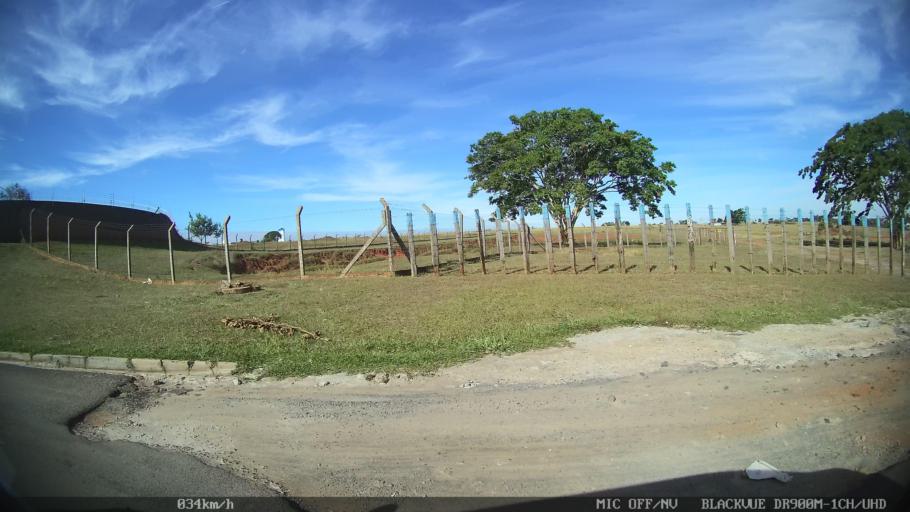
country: BR
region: Sao Paulo
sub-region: Sao Jose Do Rio Preto
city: Sao Jose do Rio Preto
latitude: -20.8113
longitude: -49.3292
